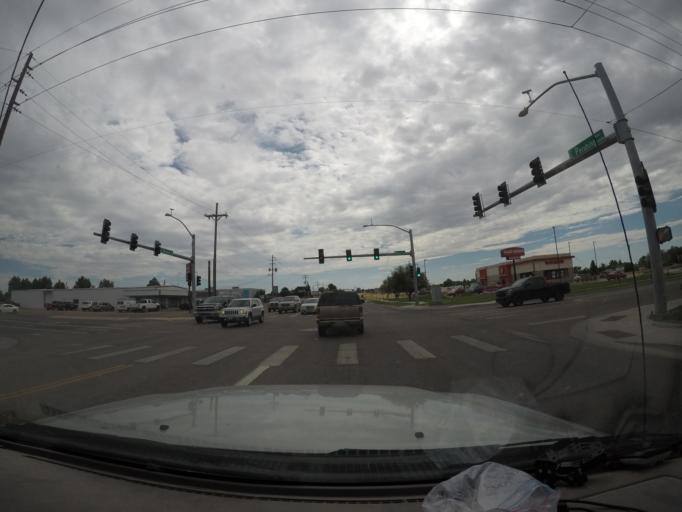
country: US
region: Wyoming
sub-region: Laramie County
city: Fox Farm-College
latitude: 41.1456
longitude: -104.7687
